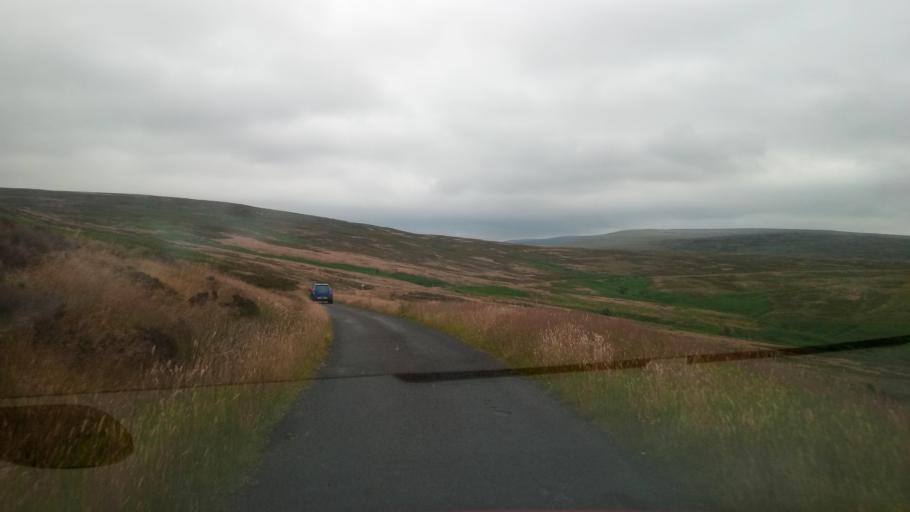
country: GB
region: Scotland
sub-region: Dumfries and Galloway
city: Langholm
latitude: 55.1661
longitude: -2.9609
